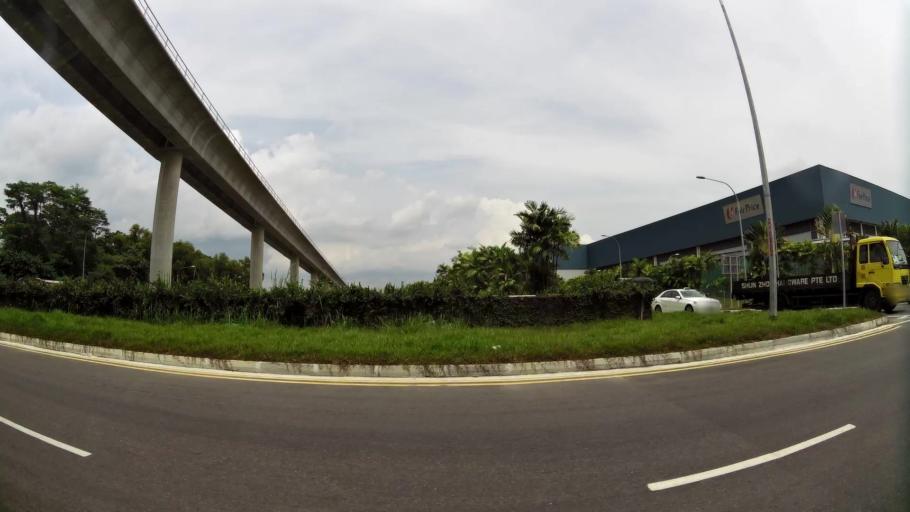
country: MY
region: Johor
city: Johor Bahru
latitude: 1.3231
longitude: 103.6637
